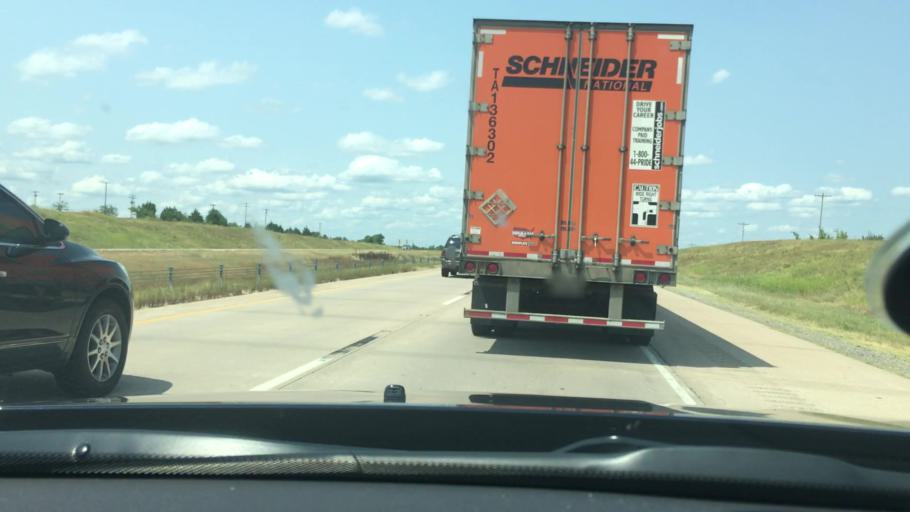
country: US
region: Oklahoma
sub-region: Carter County
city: Ardmore
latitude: 34.2084
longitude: -97.1638
